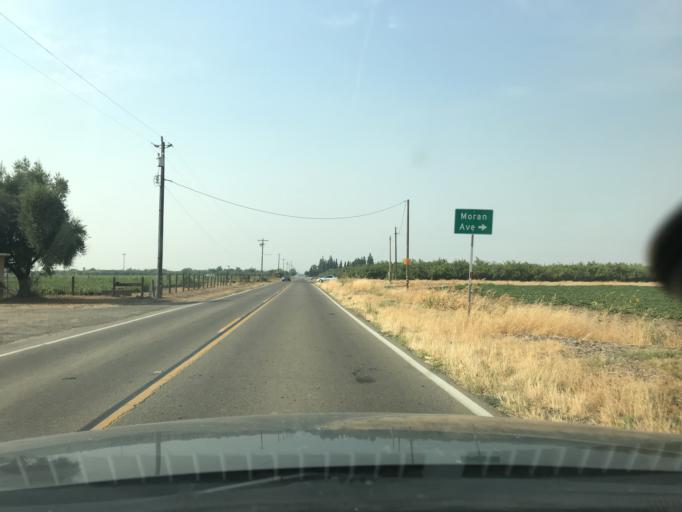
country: US
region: California
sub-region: Merced County
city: Atwater
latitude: 37.3081
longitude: -120.6147
